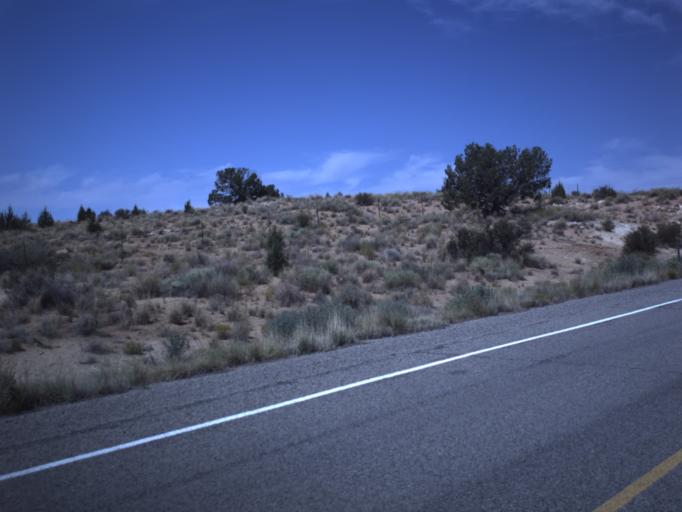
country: US
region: Colorado
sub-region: Montezuma County
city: Towaoc
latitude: 37.1855
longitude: -109.1267
